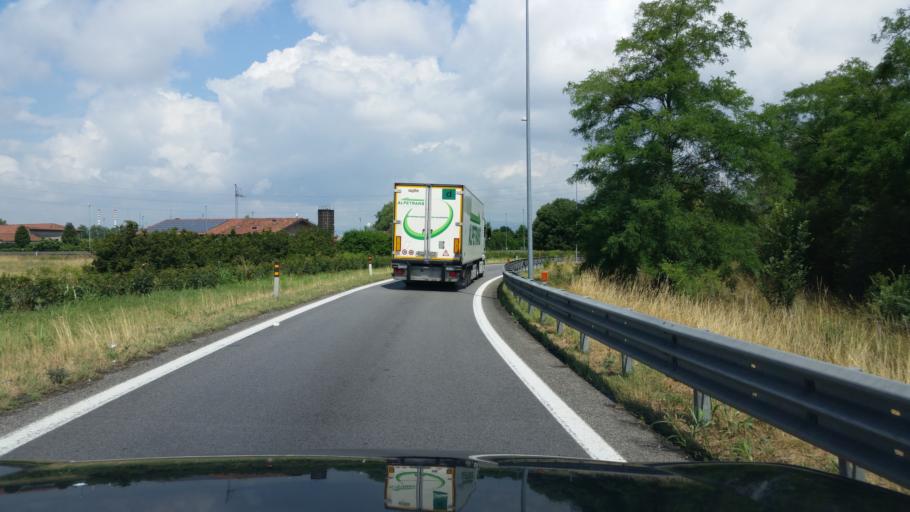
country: IT
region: Lombardy
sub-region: Provincia di Brescia
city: San Zeno Naviglio
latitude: 45.5059
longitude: 10.2365
